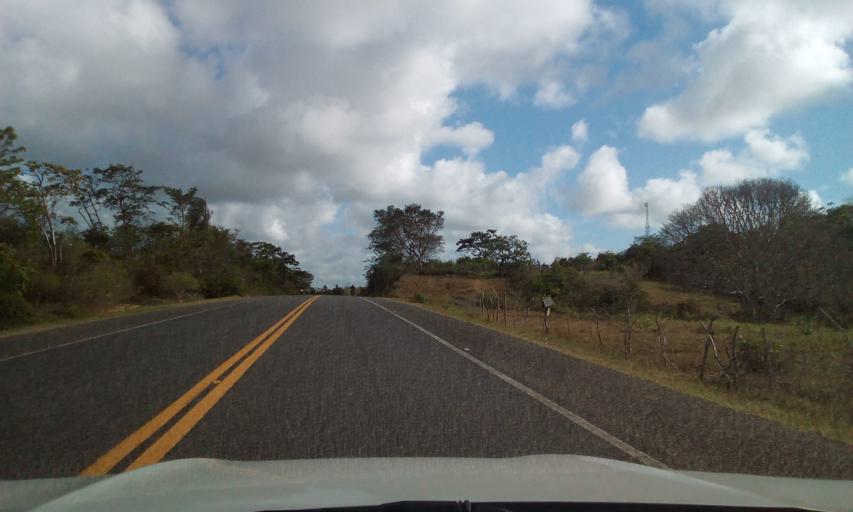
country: BR
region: Bahia
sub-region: Conde
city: Conde
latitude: -11.8046
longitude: -37.6298
